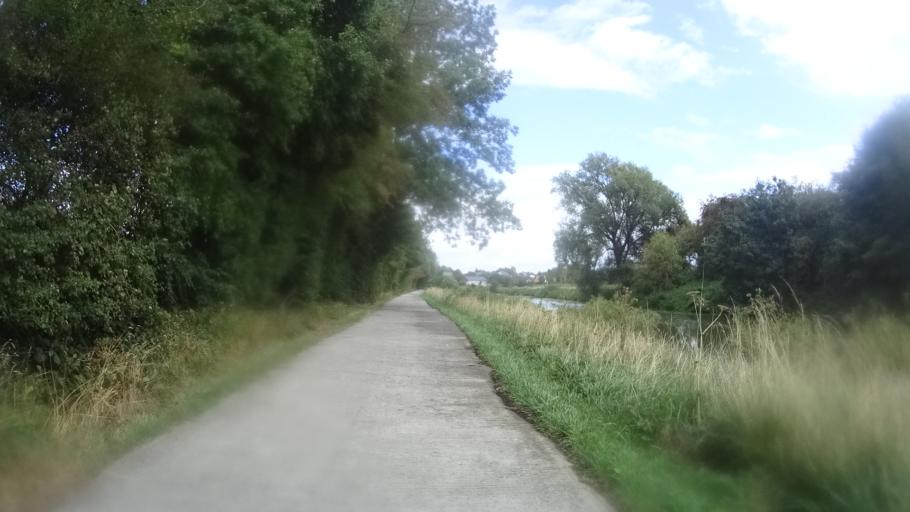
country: FR
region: Nord-Pas-de-Calais
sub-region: Departement du Nord
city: Rousies
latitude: 50.2846
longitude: 4.0094
